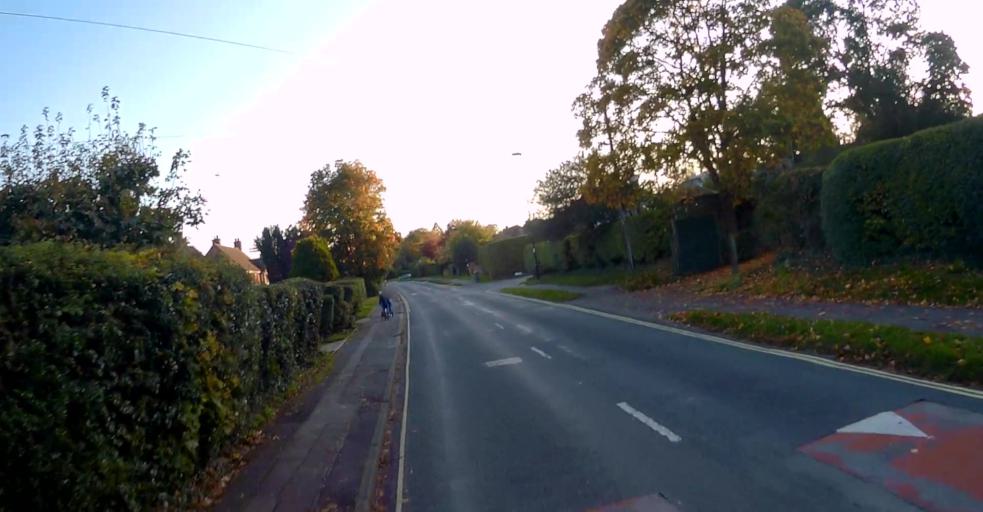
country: GB
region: England
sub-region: Hampshire
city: Basingstoke
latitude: 51.2532
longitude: -1.0872
